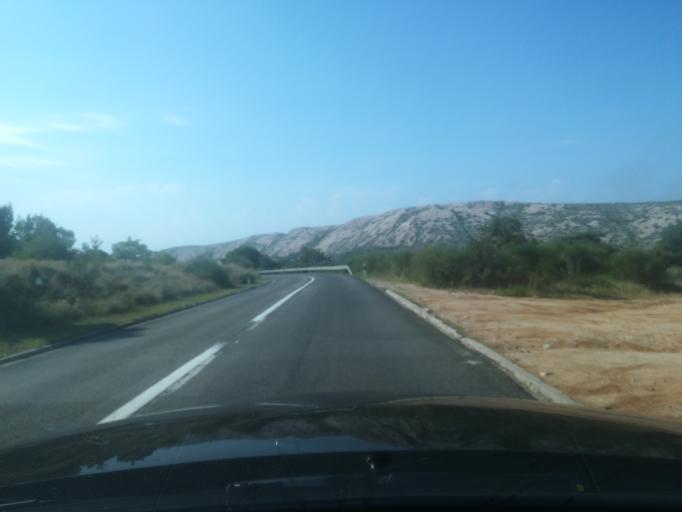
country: HR
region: Primorsko-Goranska
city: Banjol
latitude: 44.7176
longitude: 14.8248
